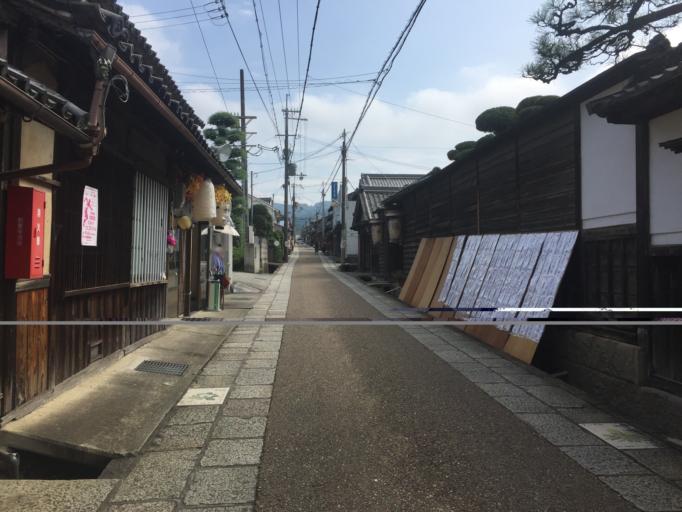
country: JP
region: Nara
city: Kashihara-shi
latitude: 34.4496
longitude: 135.7968
